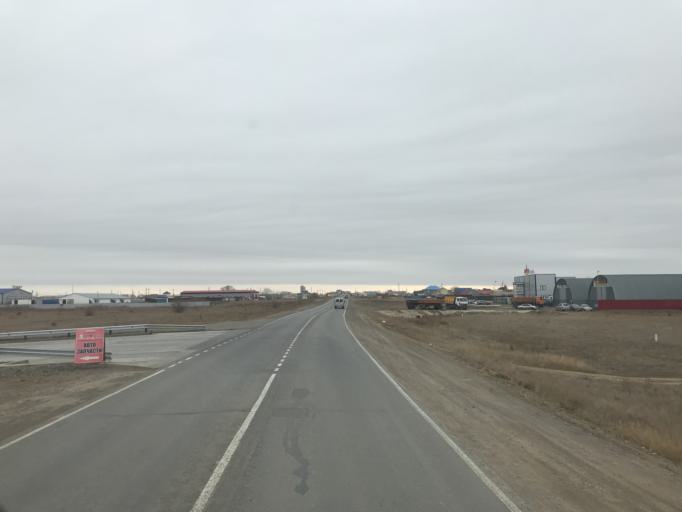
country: KZ
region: Batys Qazaqstan
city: Oral
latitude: 51.2738
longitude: 51.4004
